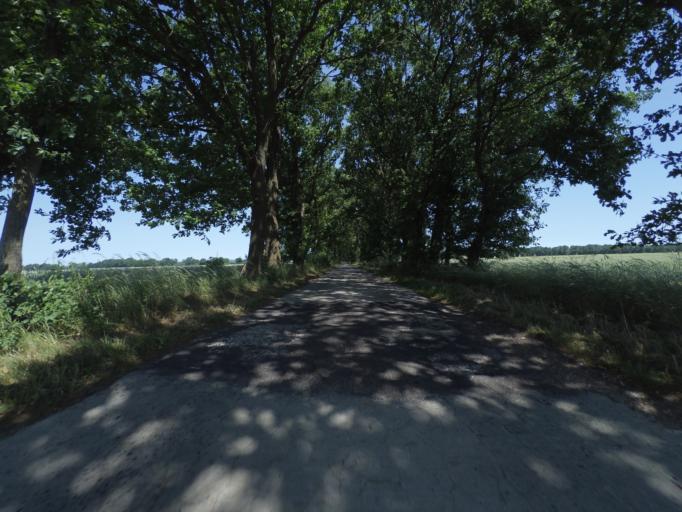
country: DE
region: Brandenburg
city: Gerdshagen
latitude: 53.2666
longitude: 12.2811
